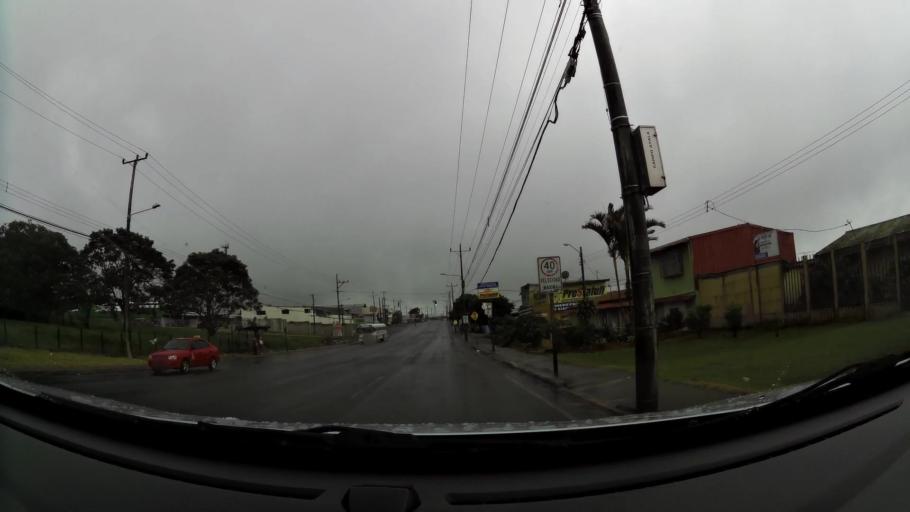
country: CR
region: Cartago
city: Paraiso
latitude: 9.8433
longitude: -83.8839
